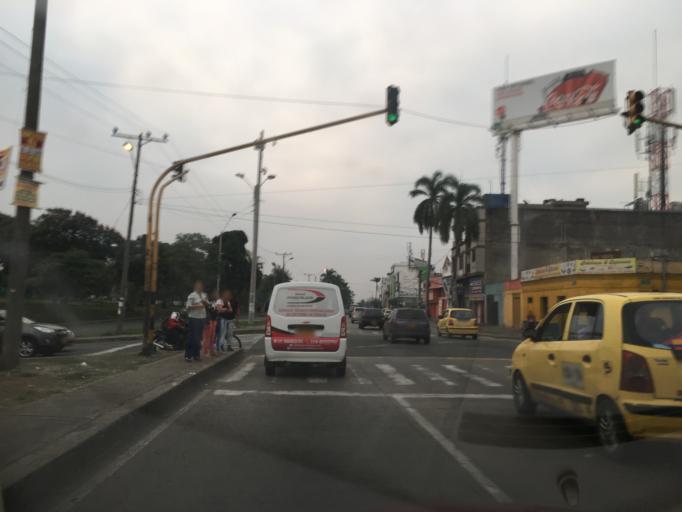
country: CO
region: Valle del Cauca
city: Cali
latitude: 3.4531
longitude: -76.5191
